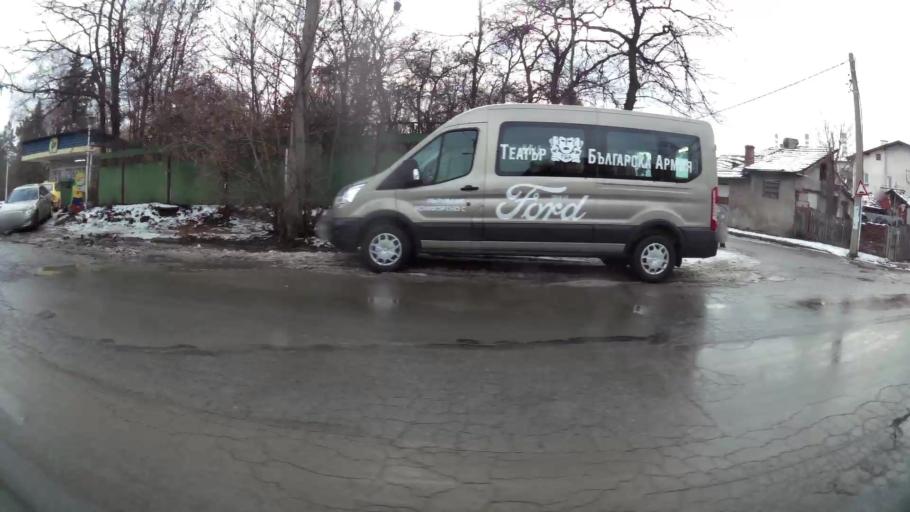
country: BG
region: Sofia-Capital
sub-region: Stolichna Obshtina
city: Sofia
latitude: 42.7210
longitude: 23.3327
